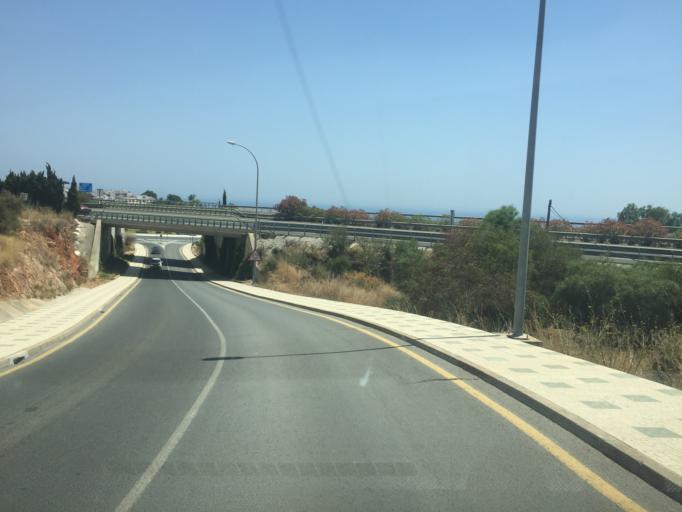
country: ES
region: Andalusia
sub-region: Provincia de Malaga
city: Nerja
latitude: 36.7605
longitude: -3.8482
